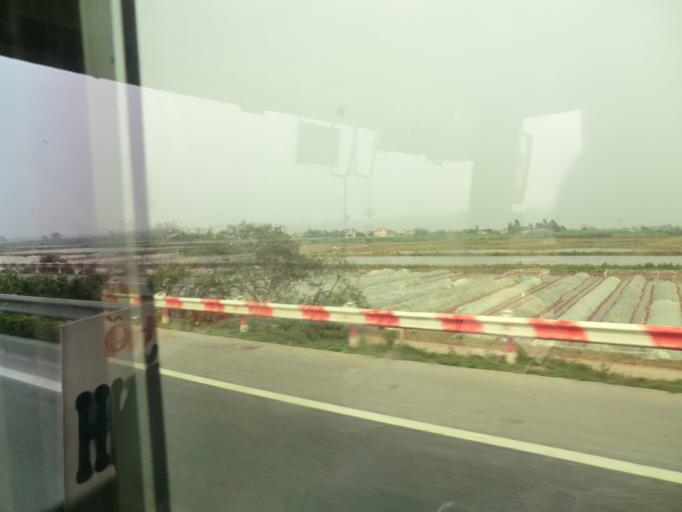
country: VN
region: Ha Noi
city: Thuong Tin
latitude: 20.8417
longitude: 105.8863
